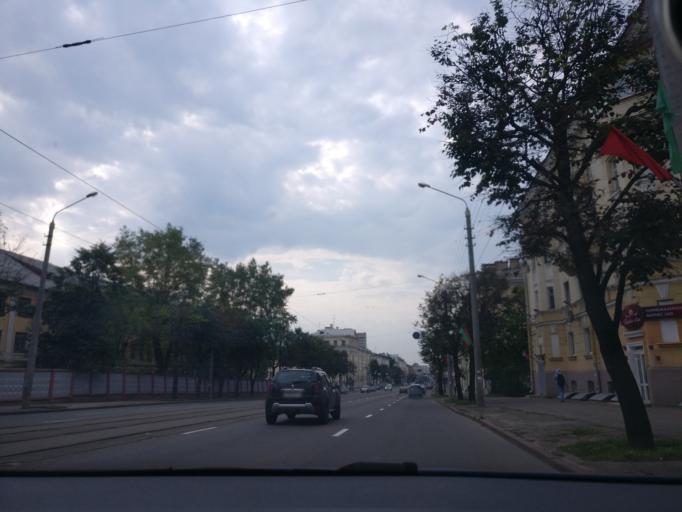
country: BY
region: Minsk
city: Minsk
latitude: 53.9318
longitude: 27.6000
